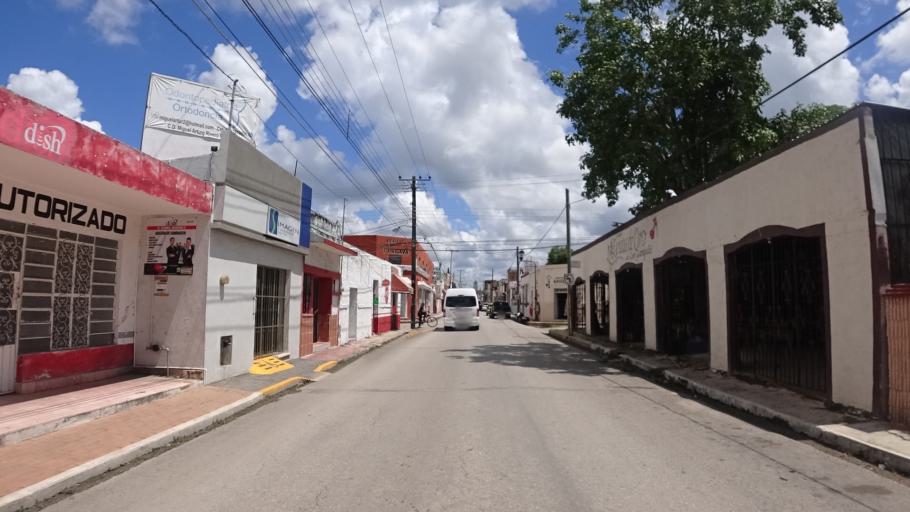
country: MX
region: Yucatan
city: Valladolid
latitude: 20.6899
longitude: -88.2090
